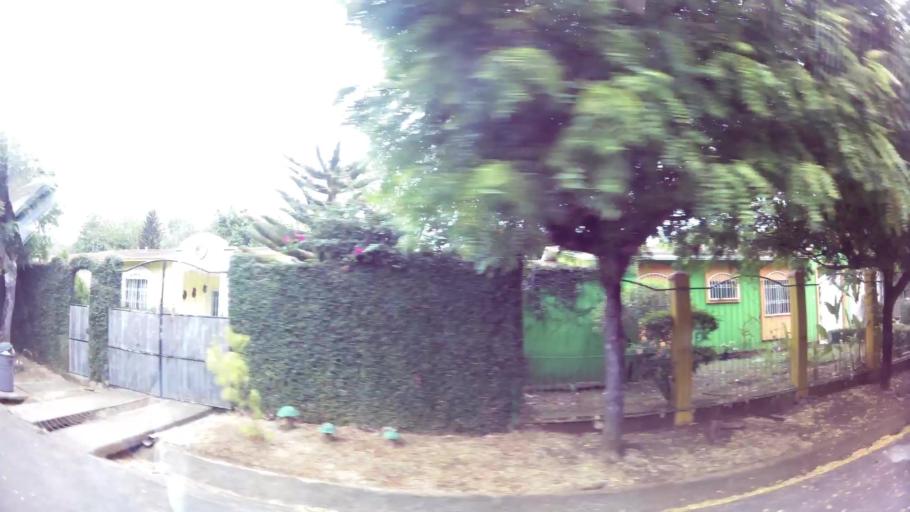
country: NI
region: Masaya
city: Ticuantepe
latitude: 12.0555
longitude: -86.1942
